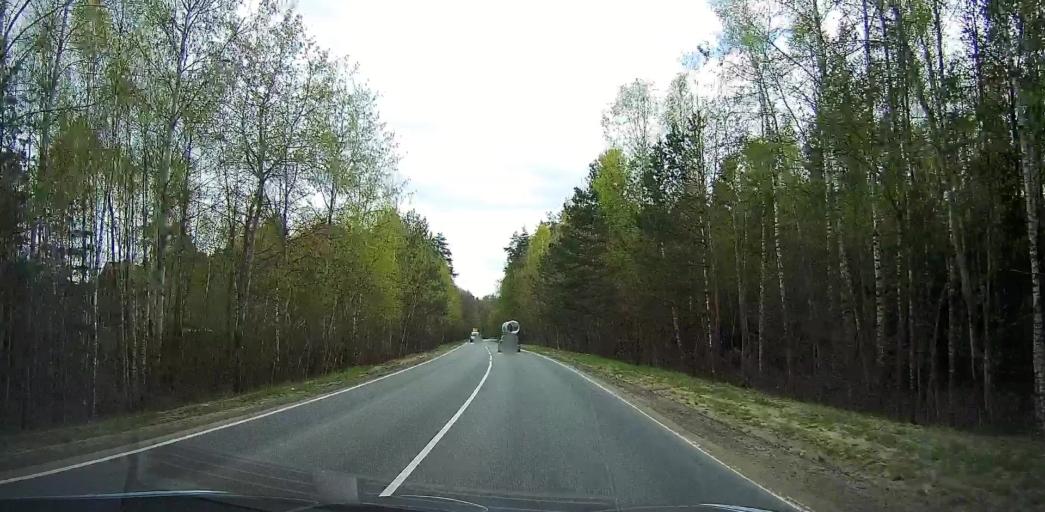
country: RU
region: Moskovskaya
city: Beloozerskiy
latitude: 55.4901
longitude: 38.4270
